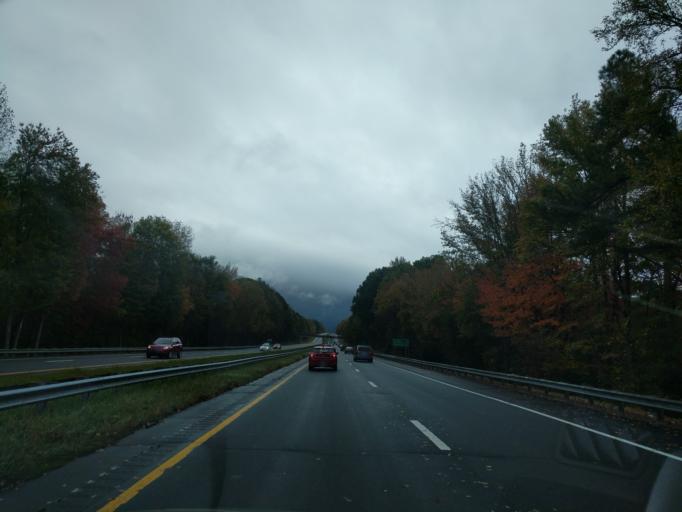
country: US
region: North Carolina
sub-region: Orange County
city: Hillsborough
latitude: 36.0556
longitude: -79.0724
